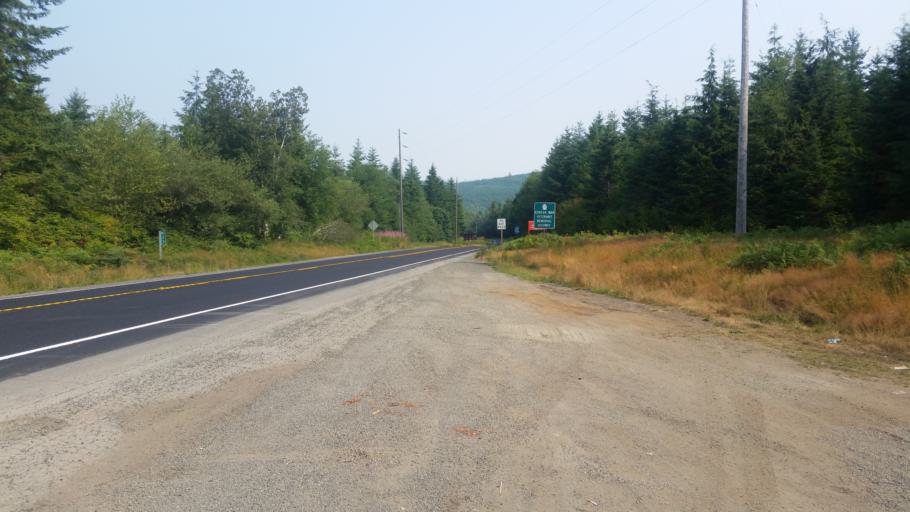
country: US
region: Washington
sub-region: Clallam County
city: Forks
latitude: 48.1783
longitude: -124.2149
